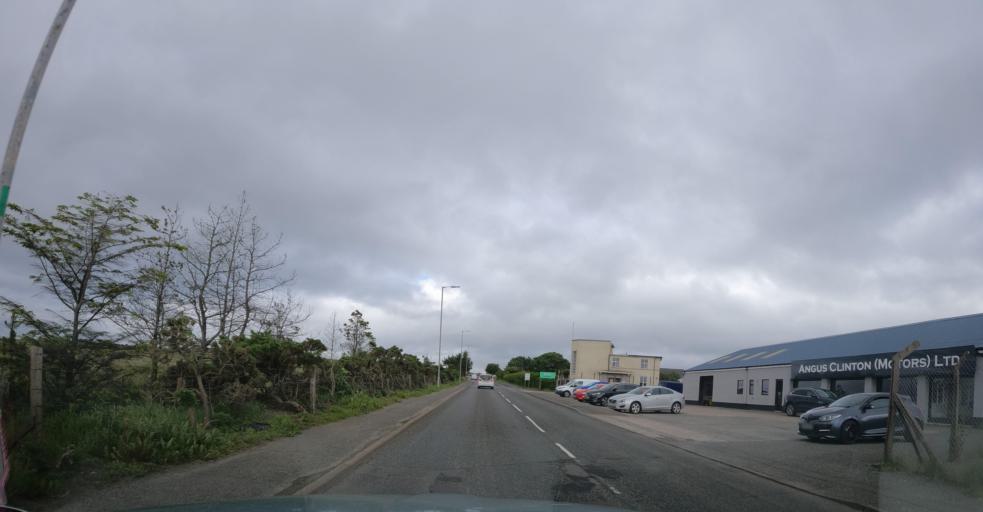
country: GB
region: Scotland
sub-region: Eilean Siar
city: Stornoway
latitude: 58.2084
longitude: -6.3714
